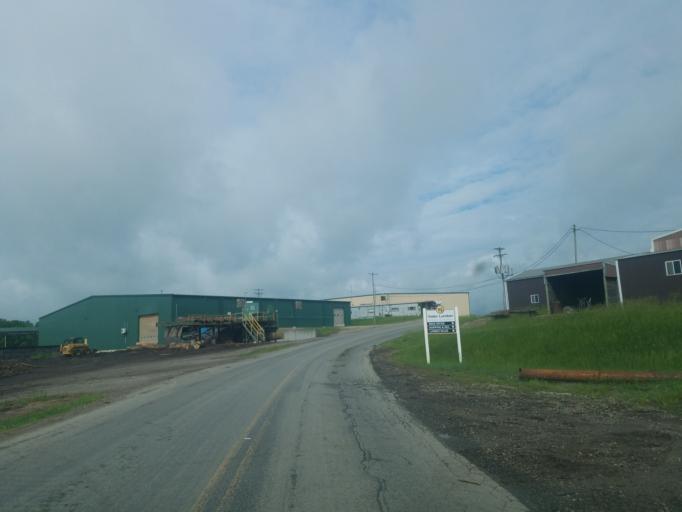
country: US
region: Ohio
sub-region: Holmes County
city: Millersburg
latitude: 40.5073
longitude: -81.8805
